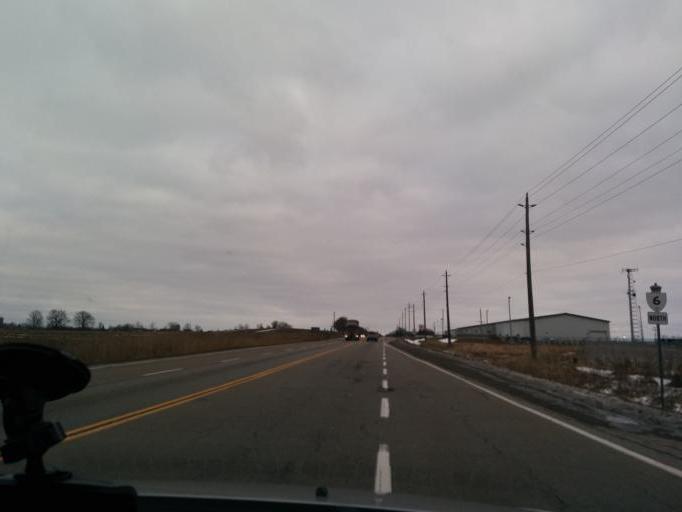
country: CA
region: Ontario
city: Ancaster
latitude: 43.0920
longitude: -79.9550
